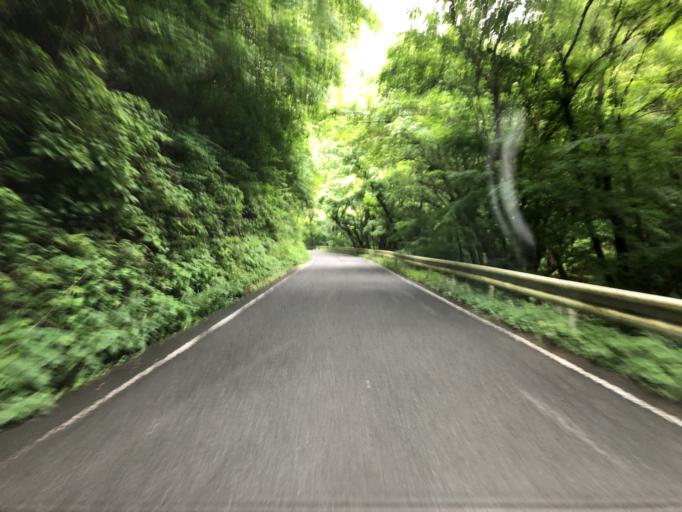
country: JP
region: Fukushima
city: Namie
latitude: 37.6901
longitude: 140.8791
